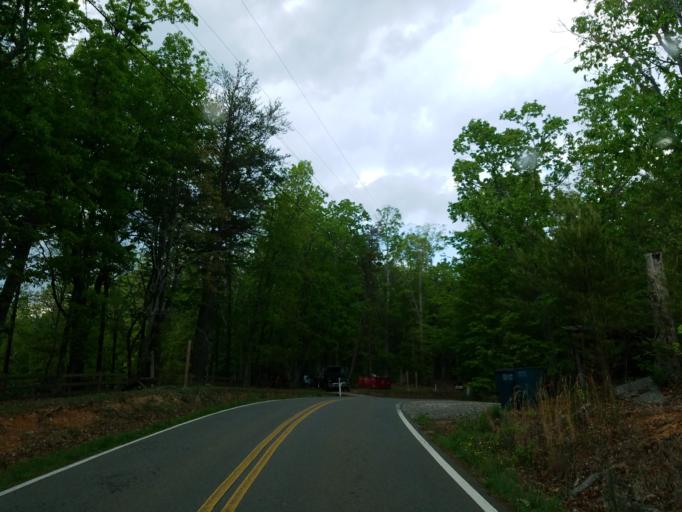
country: US
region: Georgia
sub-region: Pickens County
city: Jasper
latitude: 34.4418
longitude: -84.4791
